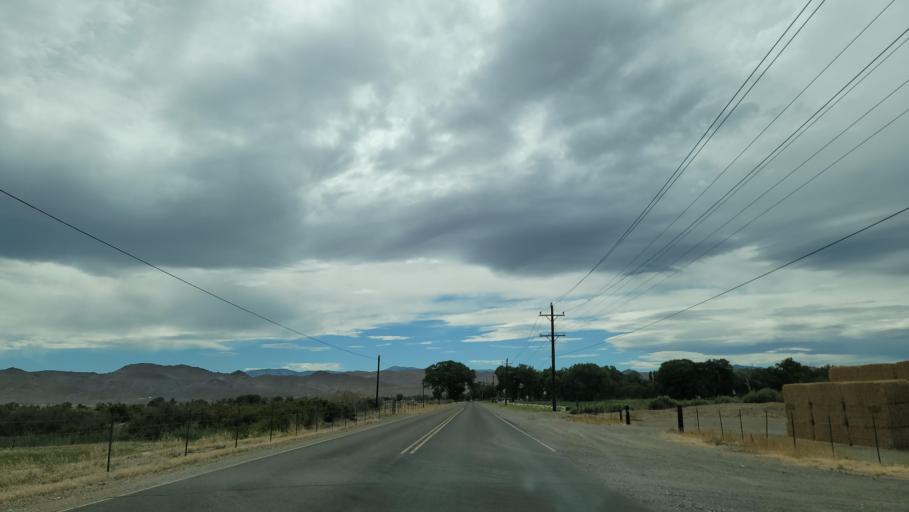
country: US
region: Nevada
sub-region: Lyon County
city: Yerington
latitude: 39.0481
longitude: -119.1722
